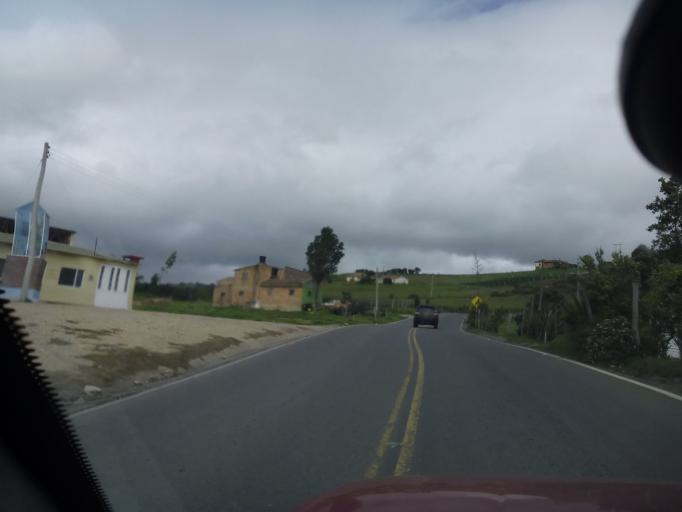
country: CO
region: Boyaca
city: Combita
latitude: 5.6299
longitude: -73.3365
